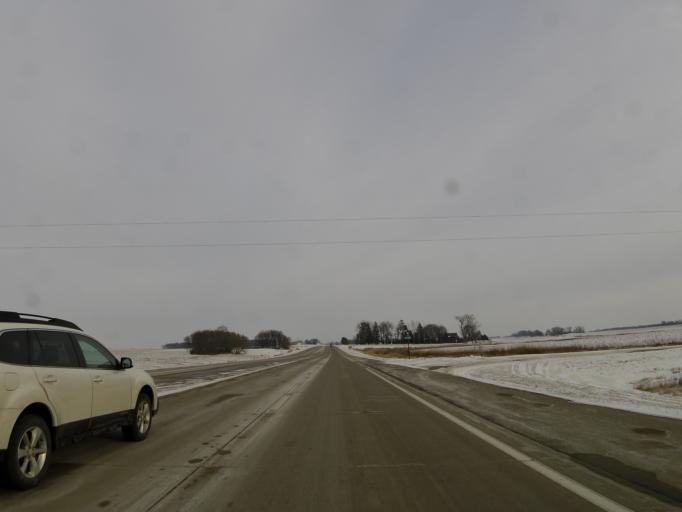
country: US
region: Minnesota
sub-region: McLeod County
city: Hutchinson
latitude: 44.8925
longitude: -94.2539
